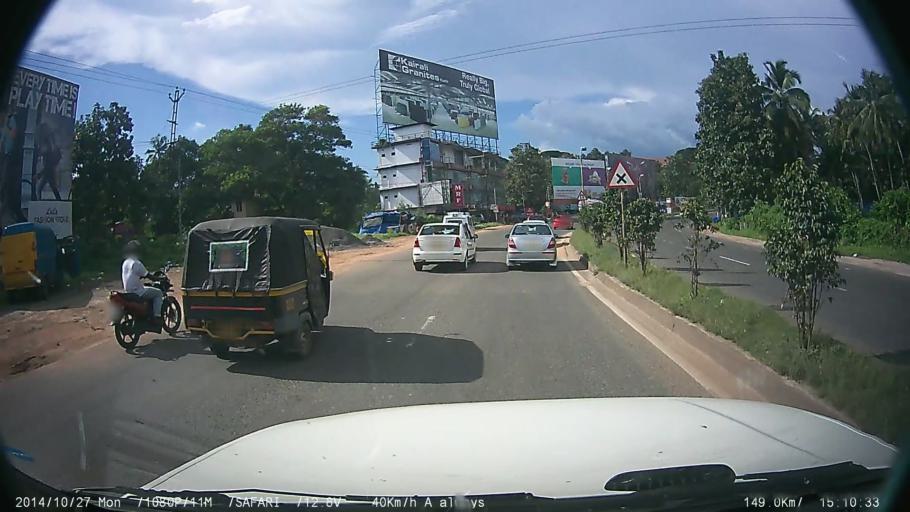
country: IN
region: Kerala
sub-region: Ernakulam
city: Aluva
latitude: 10.1234
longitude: 76.3402
